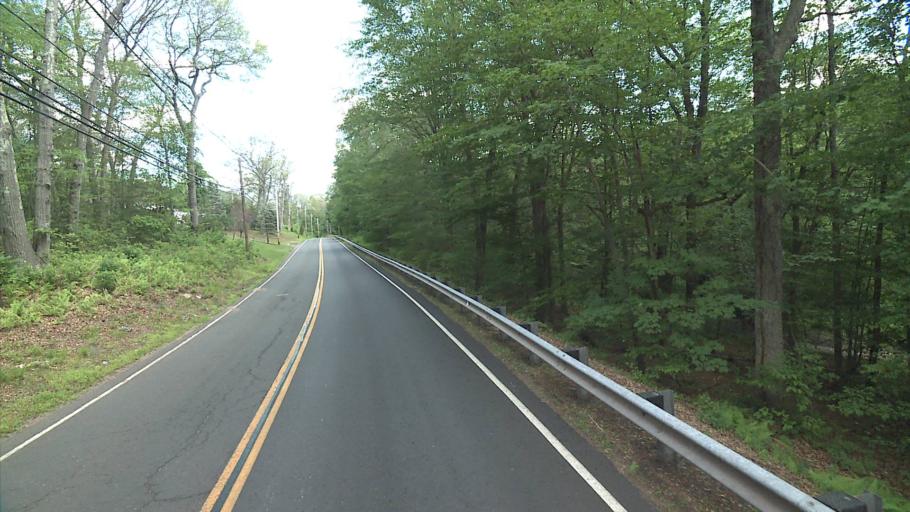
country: US
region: Connecticut
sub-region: Middlesex County
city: East Hampton
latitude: 41.5666
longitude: -72.5067
